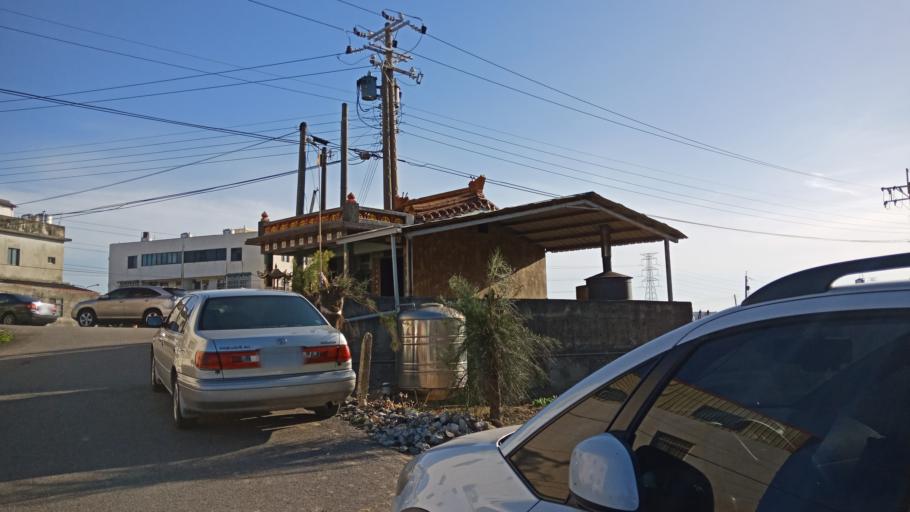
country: TW
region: Taiwan
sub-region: Miaoli
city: Miaoli
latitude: 24.4919
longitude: 120.6886
